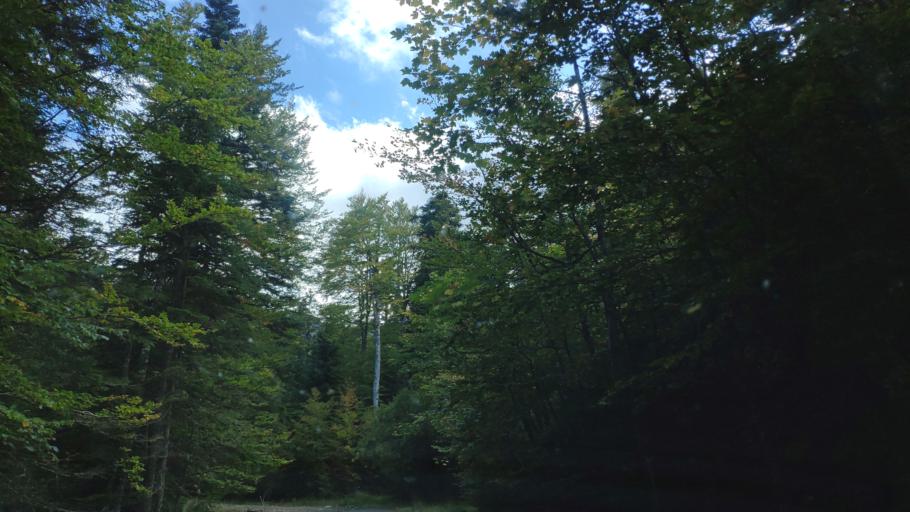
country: AL
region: Korce
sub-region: Rrethi i Devollit
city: Miras
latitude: 40.3361
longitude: 20.8999
